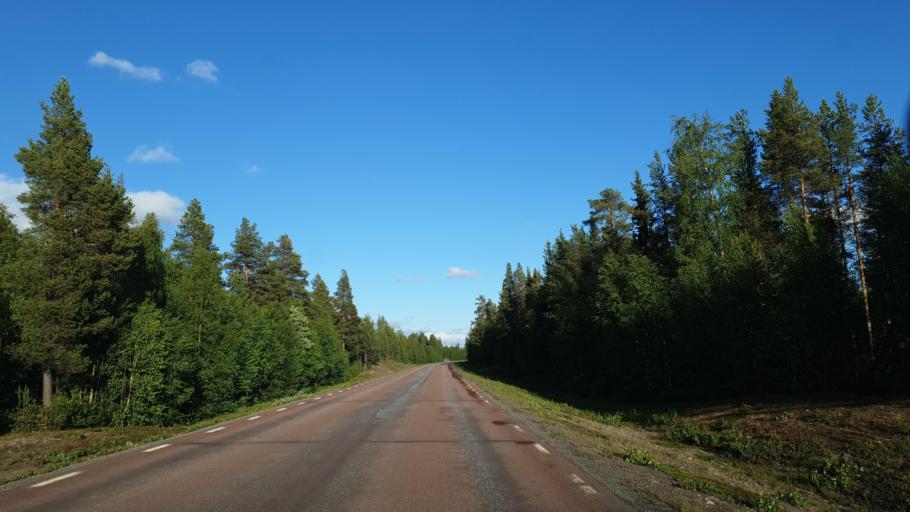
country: SE
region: Norrbotten
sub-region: Arjeplogs Kommun
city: Arjeplog
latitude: 65.9940
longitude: 18.1728
